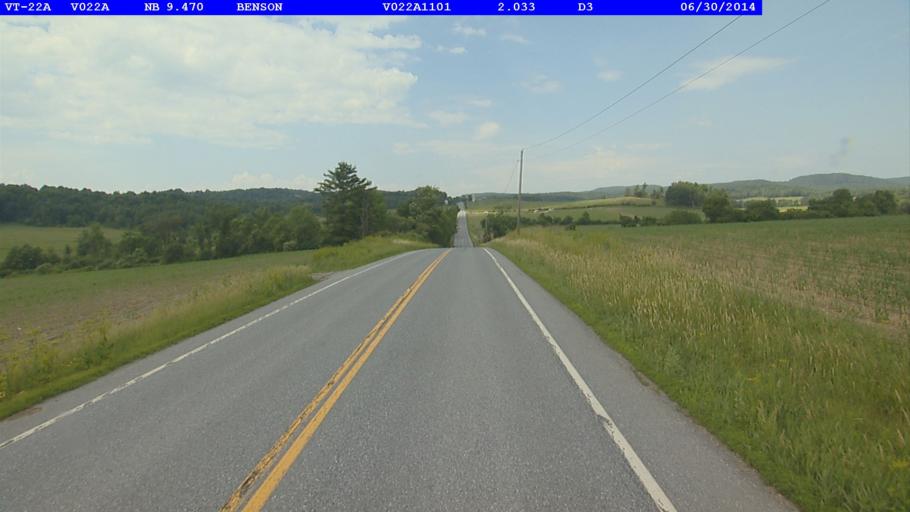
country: US
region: Vermont
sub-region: Rutland County
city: Fair Haven
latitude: 43.6979
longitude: -73.2944
